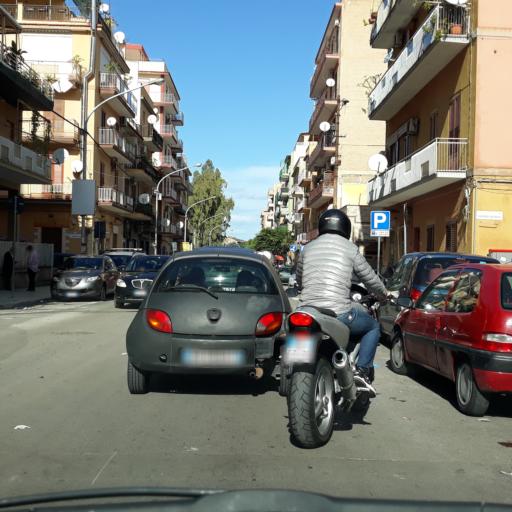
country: IT
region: Sicily
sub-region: Palermo
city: Palermo
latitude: 38.1518
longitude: 13.3707
